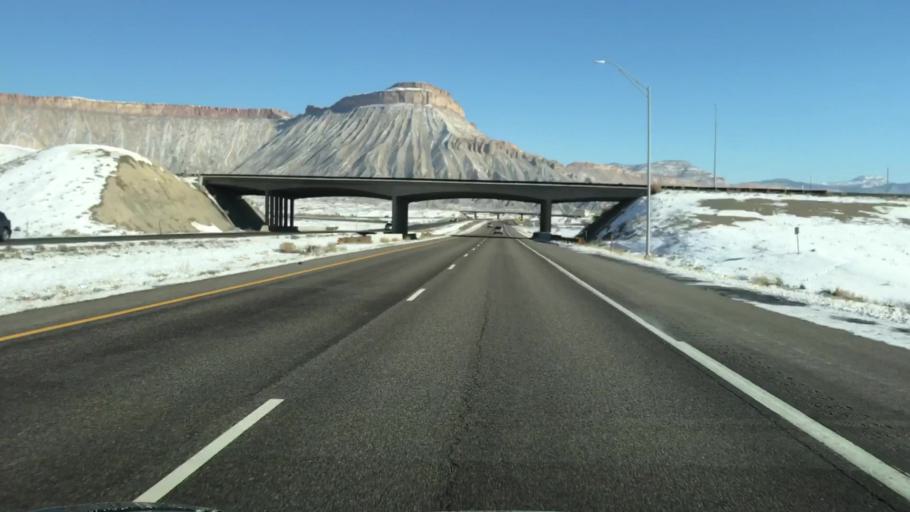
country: US
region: Colorado
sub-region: Mesa County
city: Clifton
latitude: 39.1033
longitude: -108.4484
